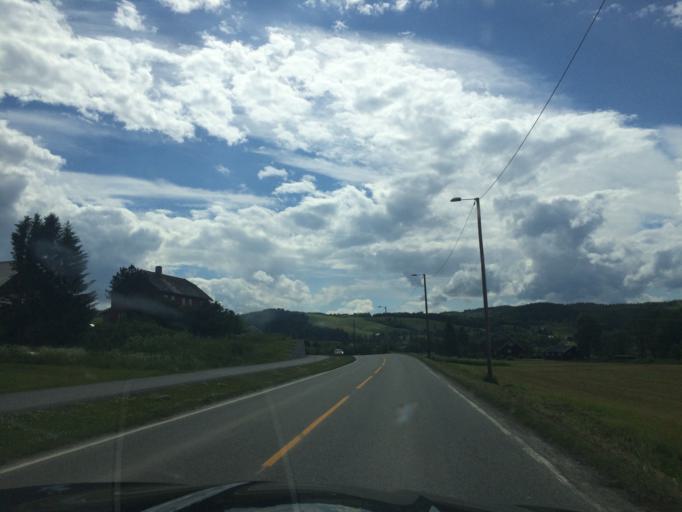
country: NO
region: Sor-Trondelag
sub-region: Selbu
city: Mebonden
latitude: 63.2486
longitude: 11.0931
